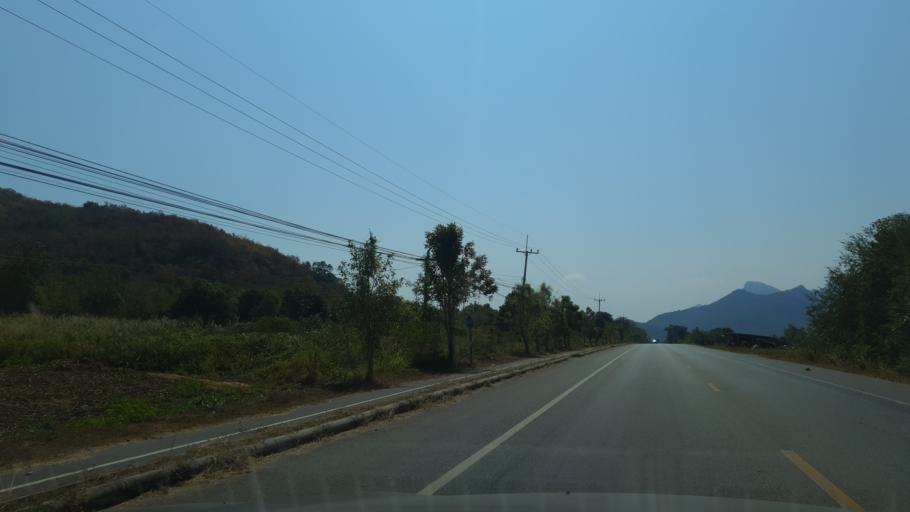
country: TH
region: Prachuap Khiri Khan
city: Pran Buri
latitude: 12.3136
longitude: 99.9613
